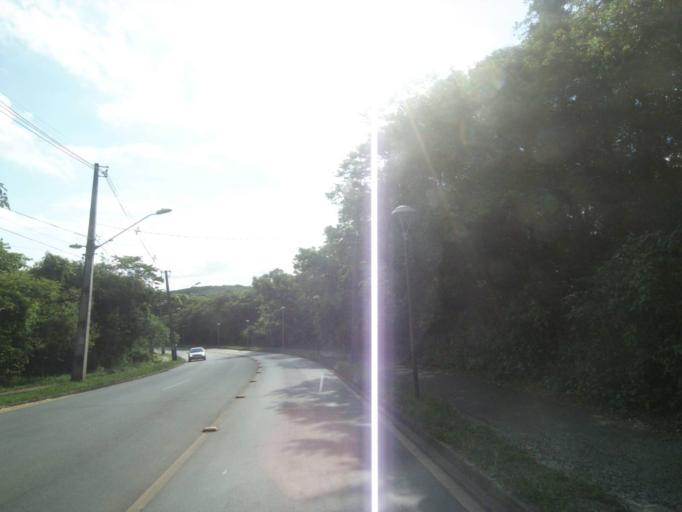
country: BR
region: Parana
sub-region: Curitiba
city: Curitiba
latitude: -25.3850
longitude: -49.2985
